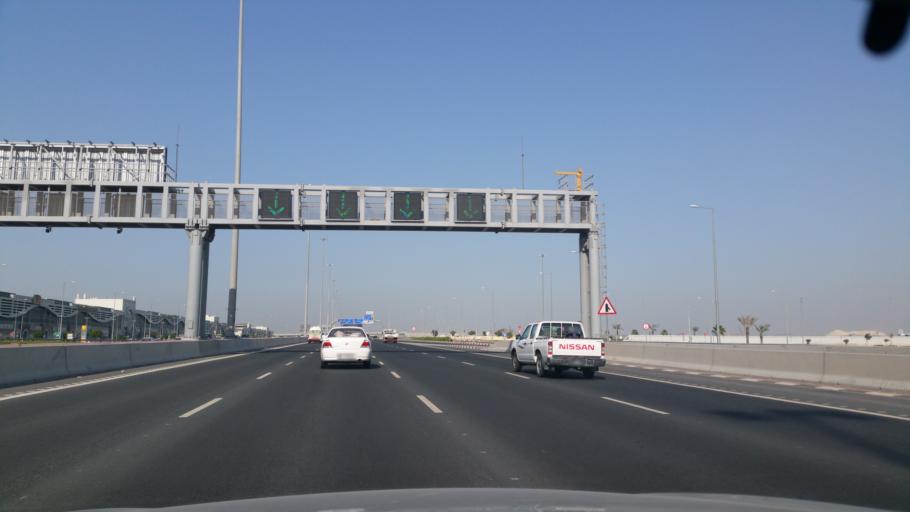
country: QA
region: Baladiyat ad Dawhah
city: Doha
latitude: 25.2146
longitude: 51.5003
